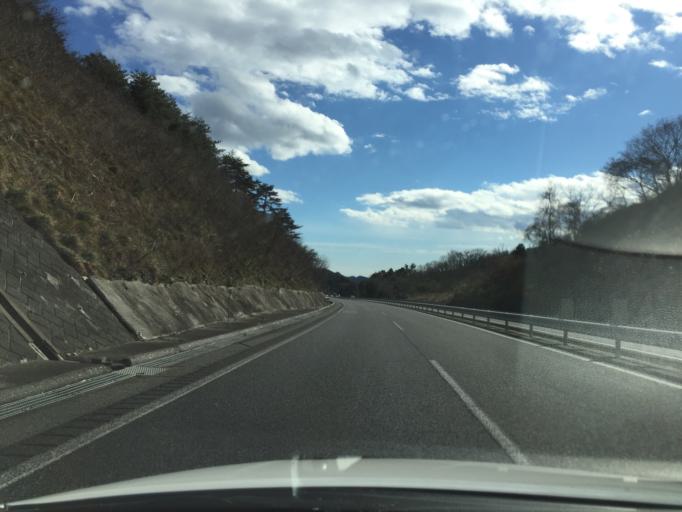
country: JP
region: Fukushima
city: Iwaki
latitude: 37.0674
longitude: 140.7929
